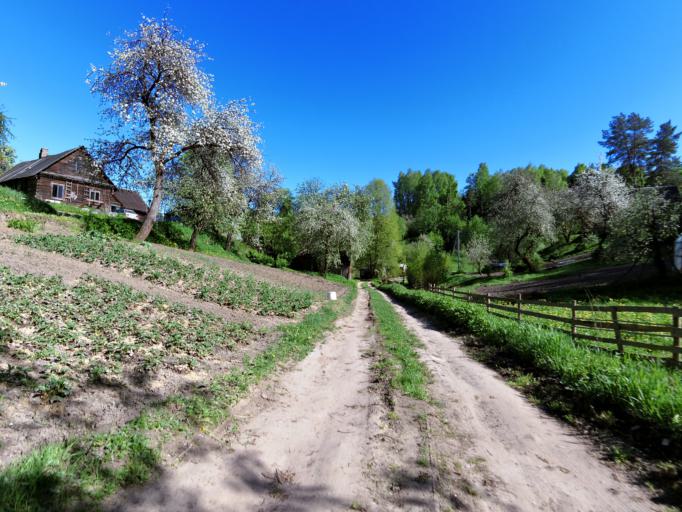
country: LT
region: Vilnius County
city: Pilaite
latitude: 54.6861
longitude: 25.1506
